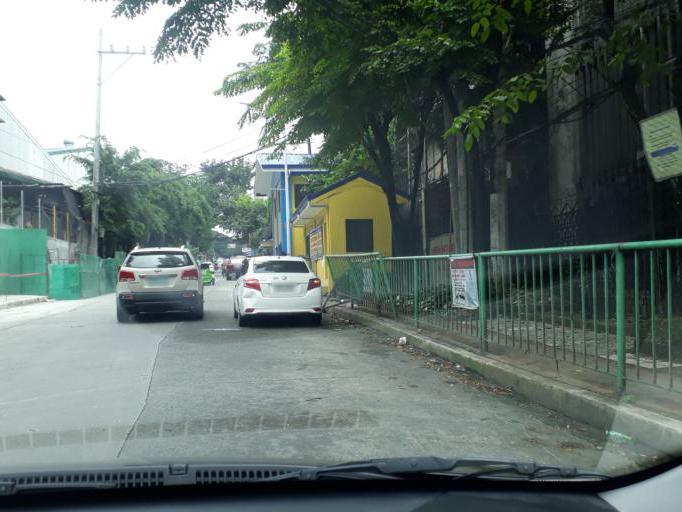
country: PH
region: Calabarzon
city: Del Monte
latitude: 14.6241
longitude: 121.0254
